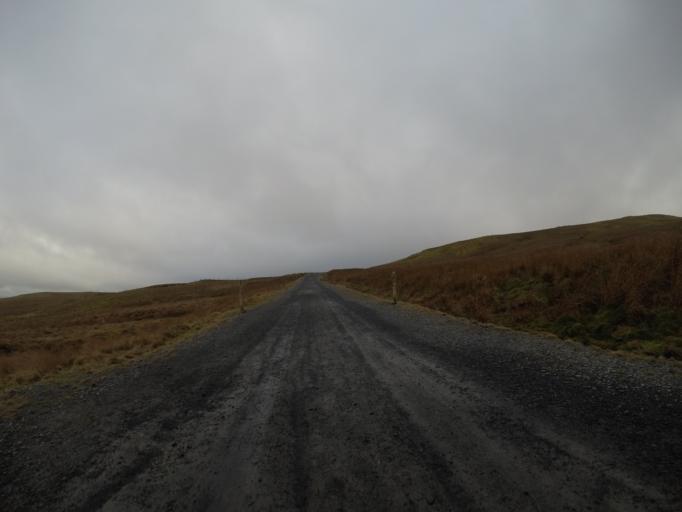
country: GB
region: Scotland
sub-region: North Ayrshire
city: Fairlie
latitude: 55.7625
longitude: -4.7921
